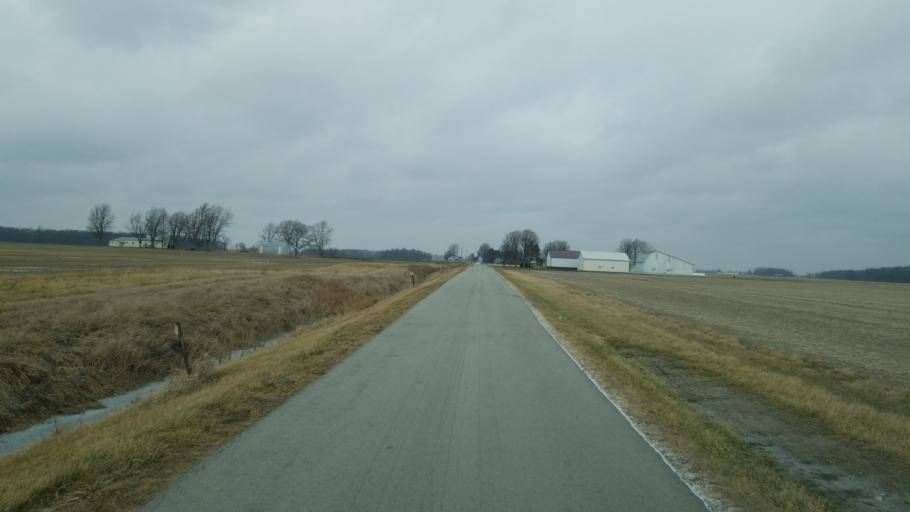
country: US
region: Ohio
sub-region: Hardin County
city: Forest
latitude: 40.7563
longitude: -83.4777
